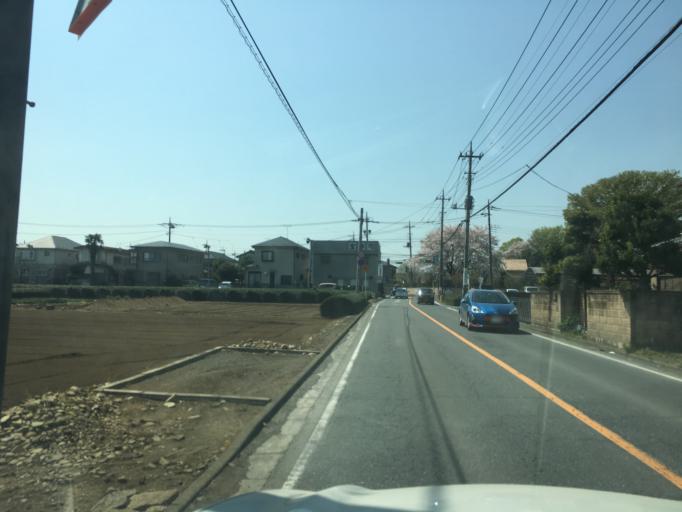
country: JP
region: Saitama
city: Sayama
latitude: 35.8378
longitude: 139.4378
